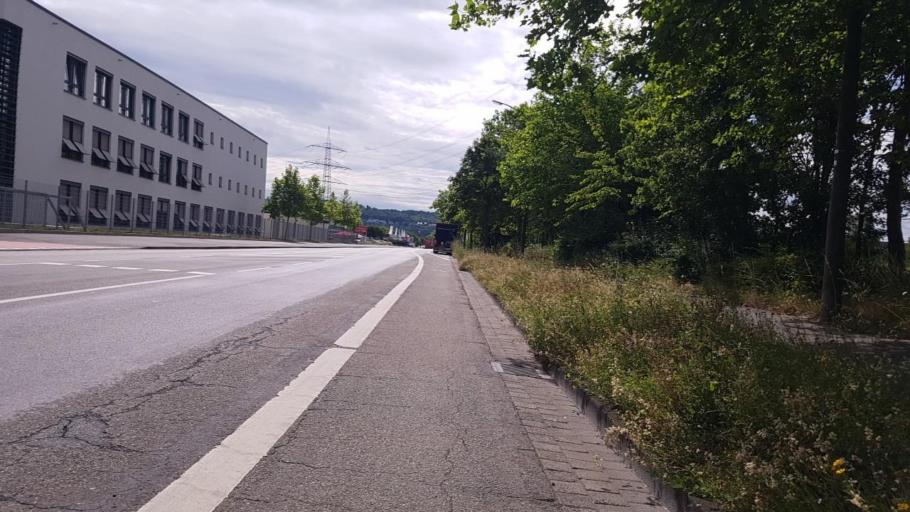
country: DE
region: Rheinland-Pfalz
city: Niederwerth
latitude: 50.3872
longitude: 7.5966
